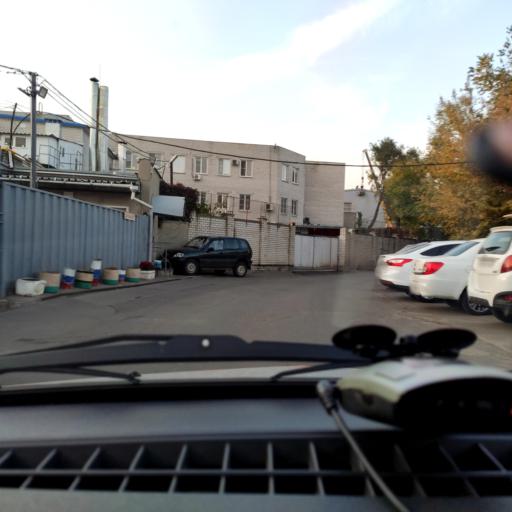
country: RU
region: Voronezj
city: Voronezh
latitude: 51.6601
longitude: 39.1371
